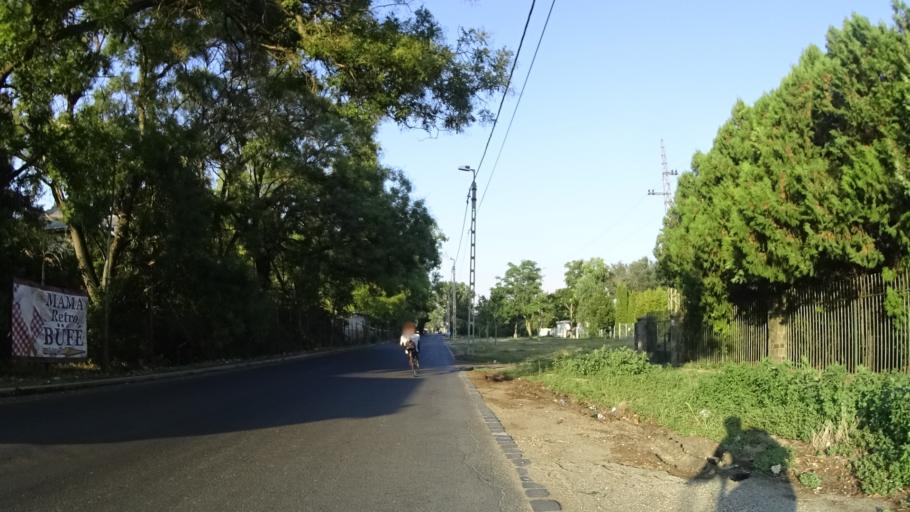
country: HU
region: Pest
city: Diosd
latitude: 47.3890
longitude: 18.9587
